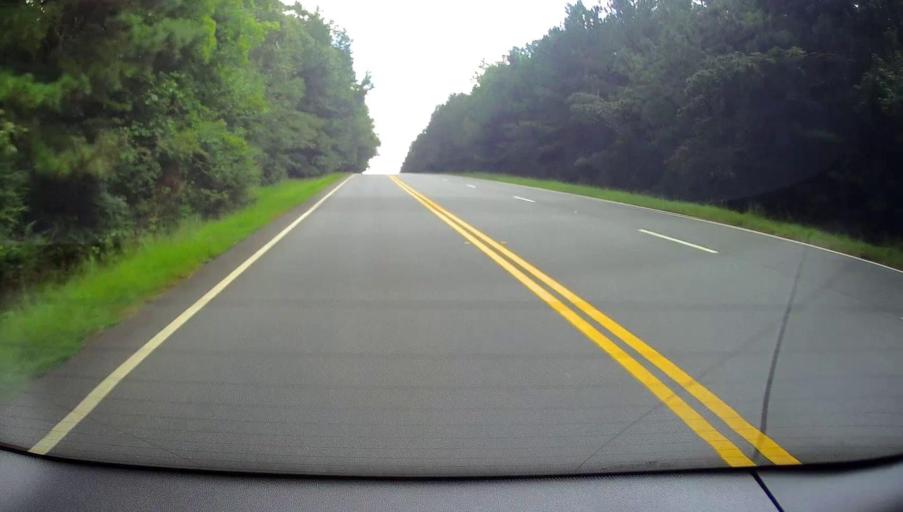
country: US
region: Georgia
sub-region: Bibb County
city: West Point
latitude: 32.8734
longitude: -83.9195
